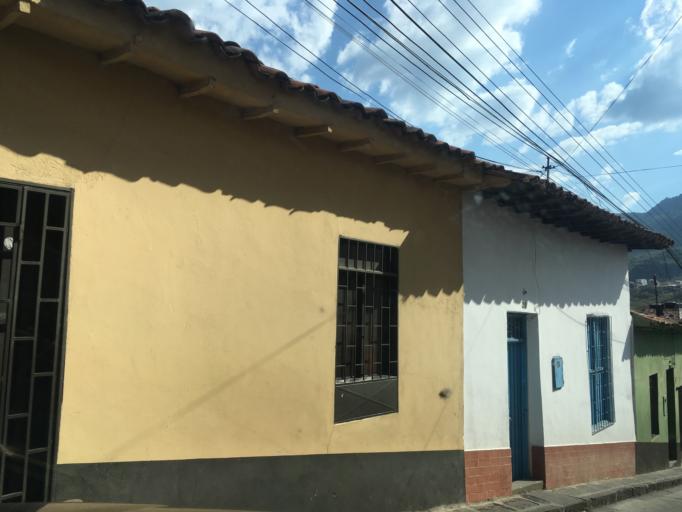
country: CO
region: Santander
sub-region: San Gil
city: San Gil
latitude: 6.5580
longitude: -73.1349
